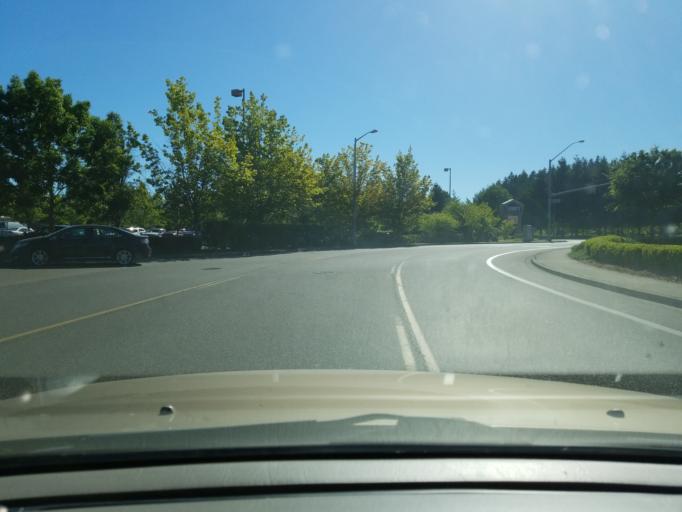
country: US
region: Oregon
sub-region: Yamhill County
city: McMinnville
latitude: 45.1924
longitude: -123.2121
